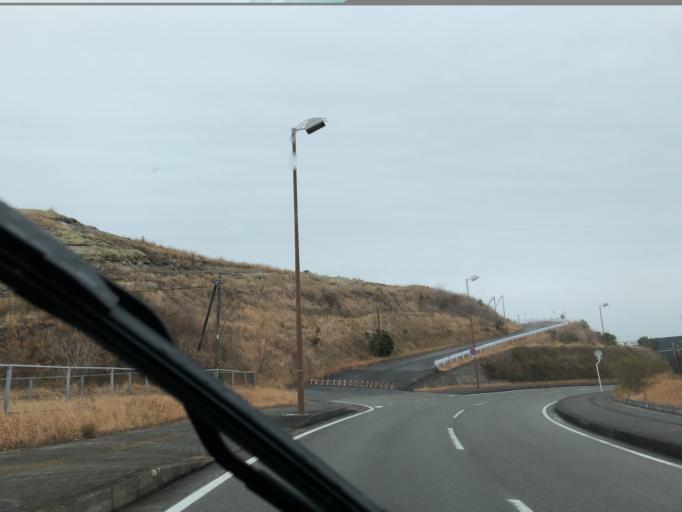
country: JP
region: Wakayama
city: Tanabe
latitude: 33.6633
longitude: 135.3591
